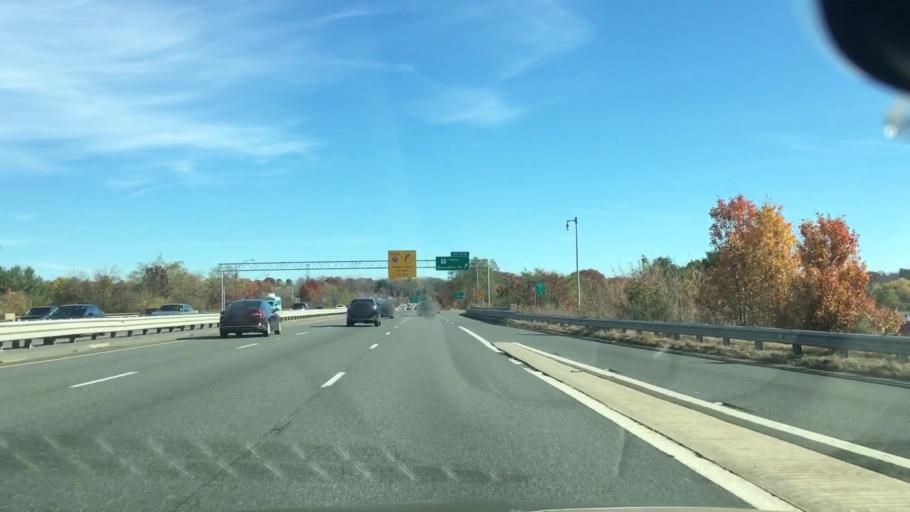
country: US
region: Massachusetts
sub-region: Hampden County
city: Chicopee
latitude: 42.1361
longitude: -72.6267
